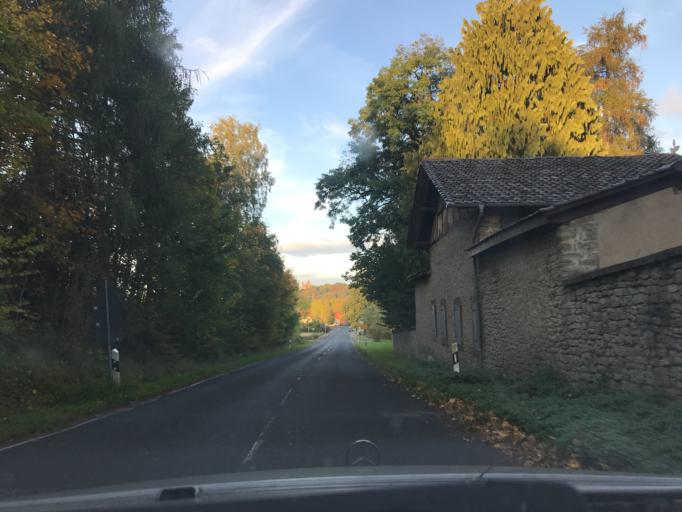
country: DE
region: Lower Saxony
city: Gemeinde Friedland
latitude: 51.4066
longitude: 9.8946
